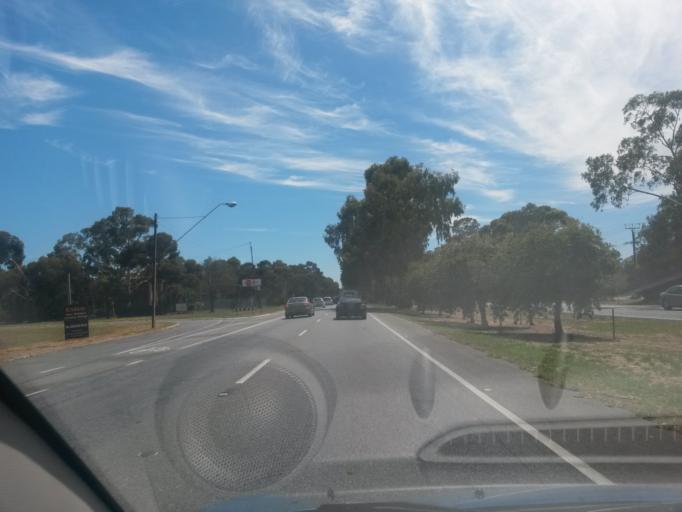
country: AU
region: South Australia
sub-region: Salisbury
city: Salisbury
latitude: -34.7865
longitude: 138.6513
